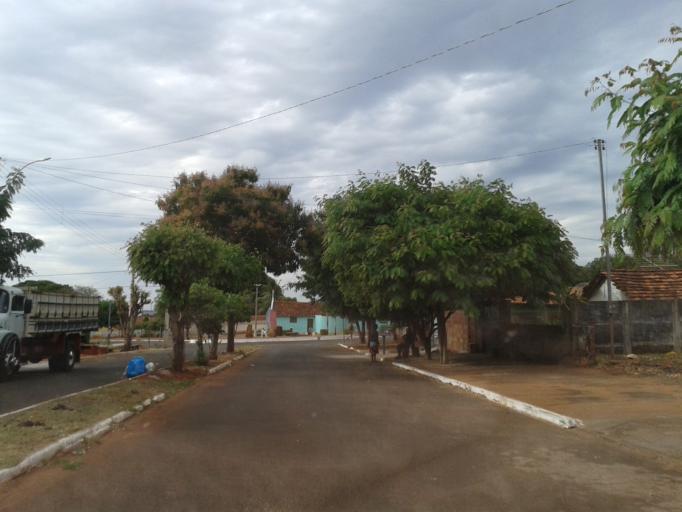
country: BR
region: Minas Gerais
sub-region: Santa Vitoria
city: Santa Vitoria
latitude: -18.8327
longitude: -50.1376
